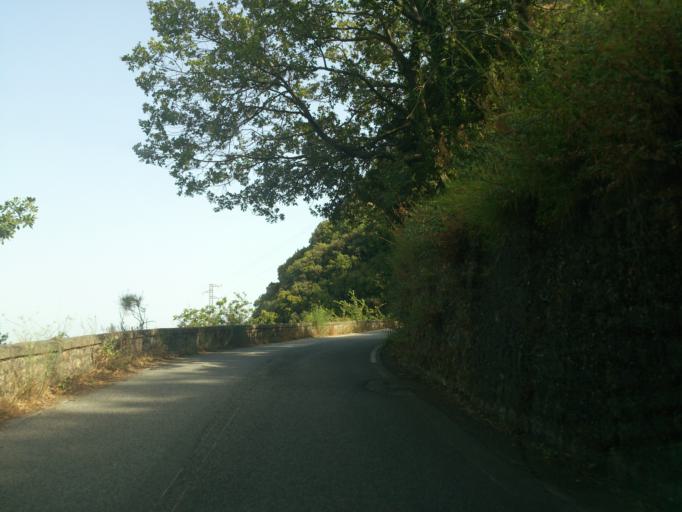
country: IT
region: Calabria
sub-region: Provincia di Reggio Calabria
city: Pazzano
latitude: 38.4748
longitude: 16.4504
